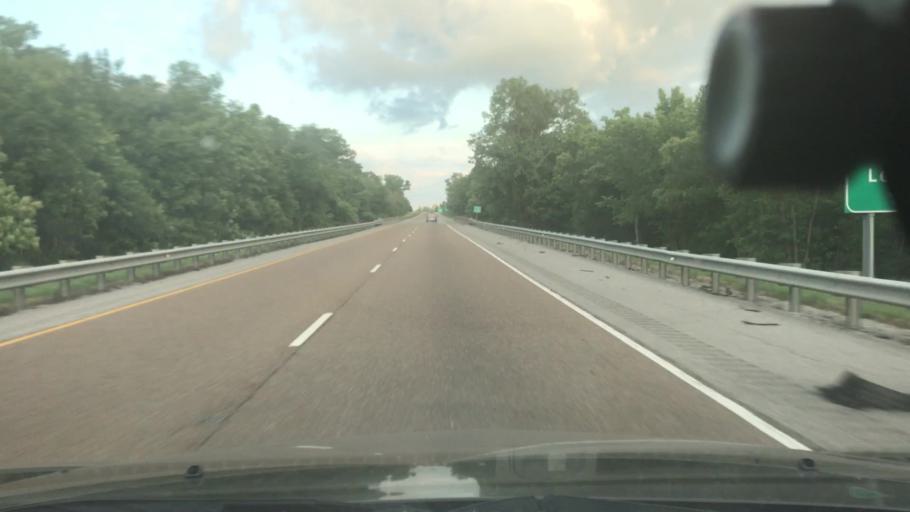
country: US
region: Illinois
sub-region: Saint Clair County
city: Scott Air Force Base
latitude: 38.5595
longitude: -89.8286
